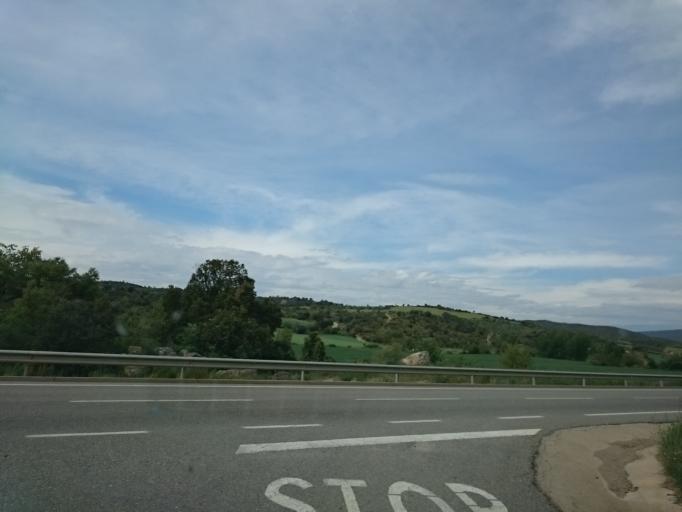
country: ES
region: Catalonia
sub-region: Provincia de Lleida
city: Tora de Riubregos
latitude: 41.8068
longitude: 1.3132
